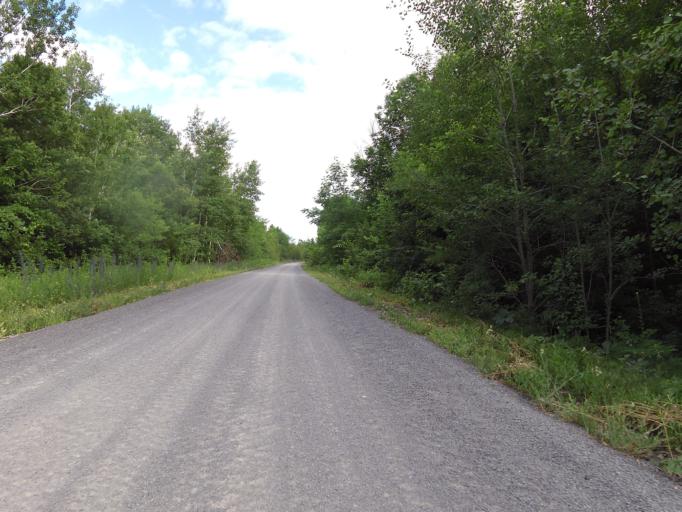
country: CA
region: Ontario
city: Arnprior
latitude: 45.3023
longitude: -76.2672
